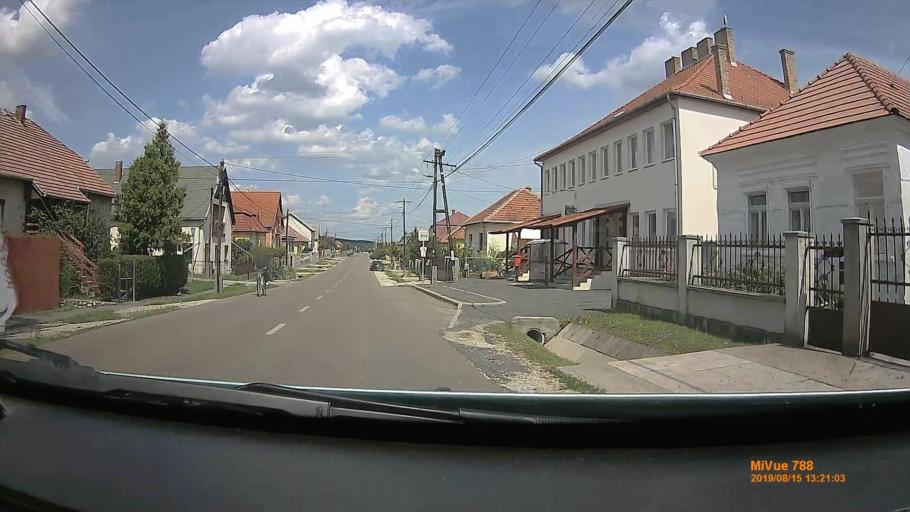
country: HU
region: Borsod-Abauj-Zemplen
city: Kazincbarcika
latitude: 48.1793
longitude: 20.6393
